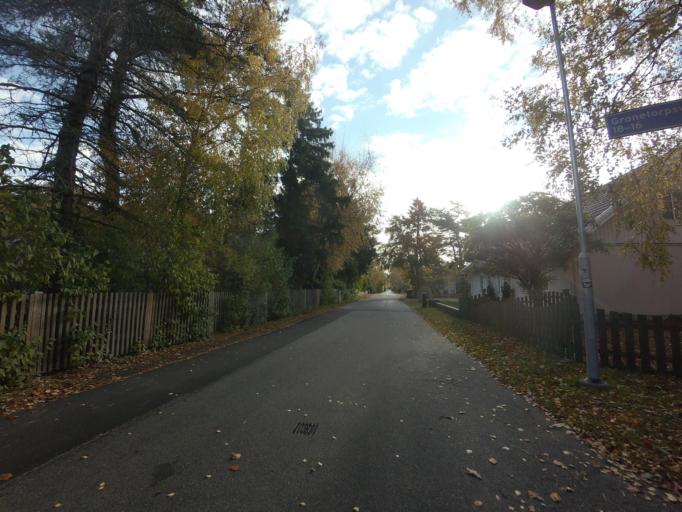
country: SE
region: Skane
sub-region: Vellinge Kommun
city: Hollviken
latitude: 55.4175
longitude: 12.9695
